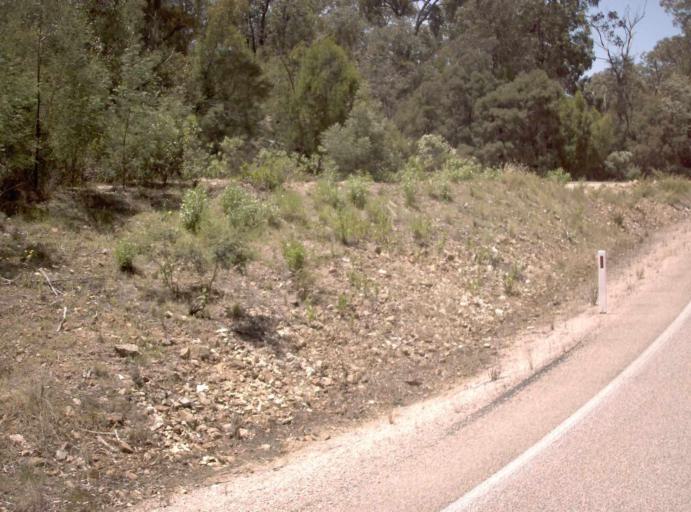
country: AU
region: Victoria
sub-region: East Gippsland
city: Lakes Entrance
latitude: -37.5645
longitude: 147.8878
